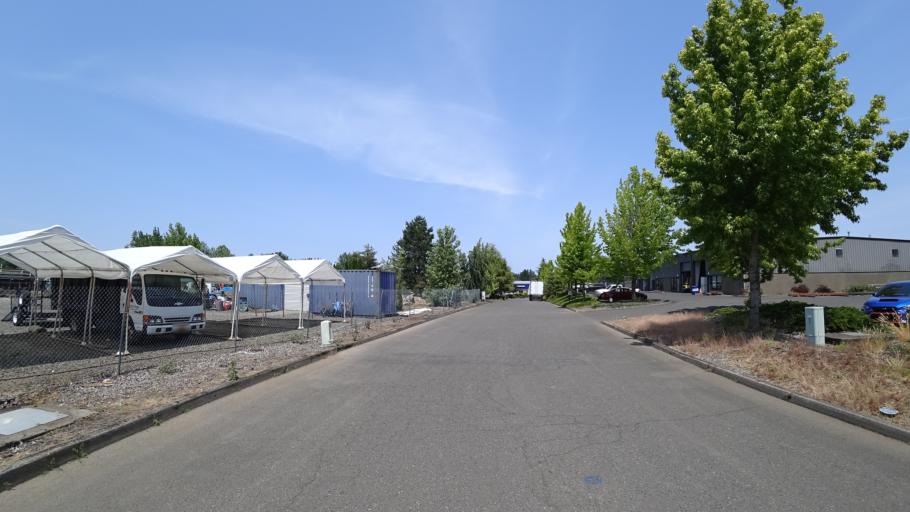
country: US
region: Oregon
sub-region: Washington County
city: Hillsboro
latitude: 45.4996
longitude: -122.9449
